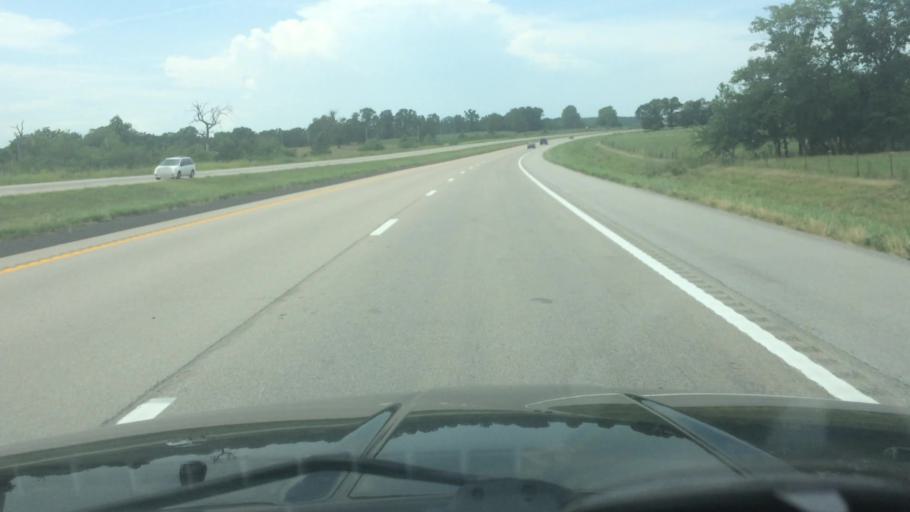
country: US
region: Missouri
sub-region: Polk County
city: Humansville
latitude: 37.8208
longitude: -93.6144
